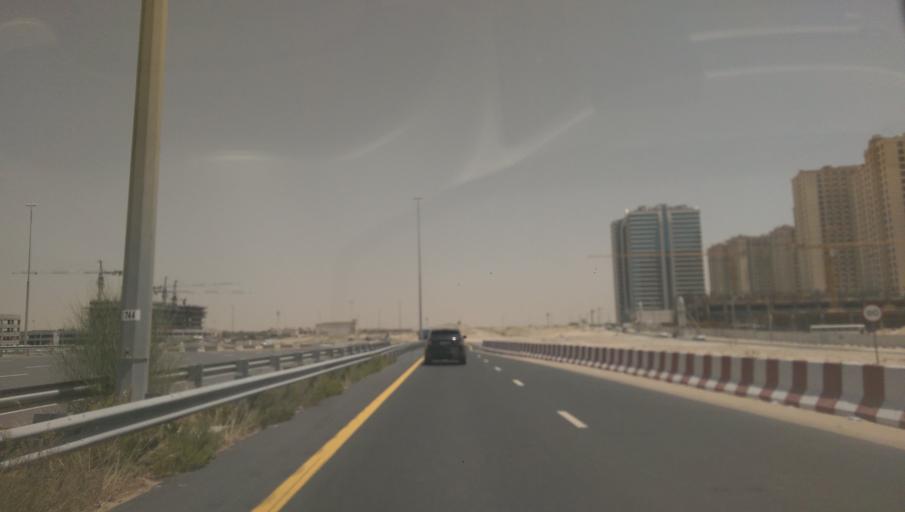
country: AE
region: Dubai
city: Dubai
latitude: 25.0389
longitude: 55.2021
